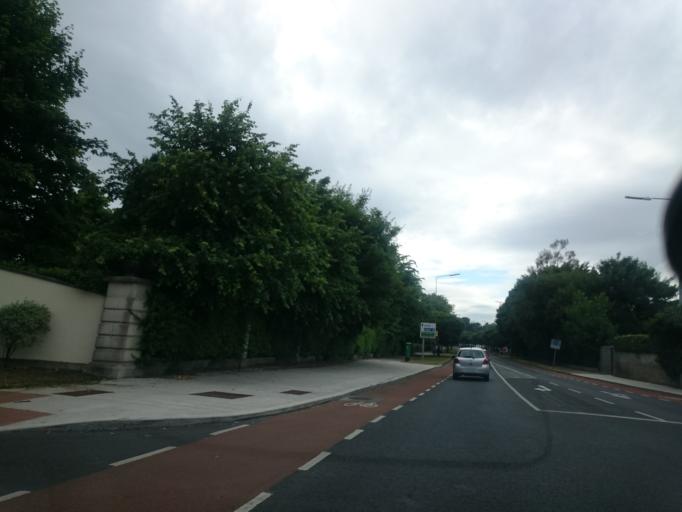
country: IE
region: Leinster
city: Rathgar
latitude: 53.3034
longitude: -6.2712
